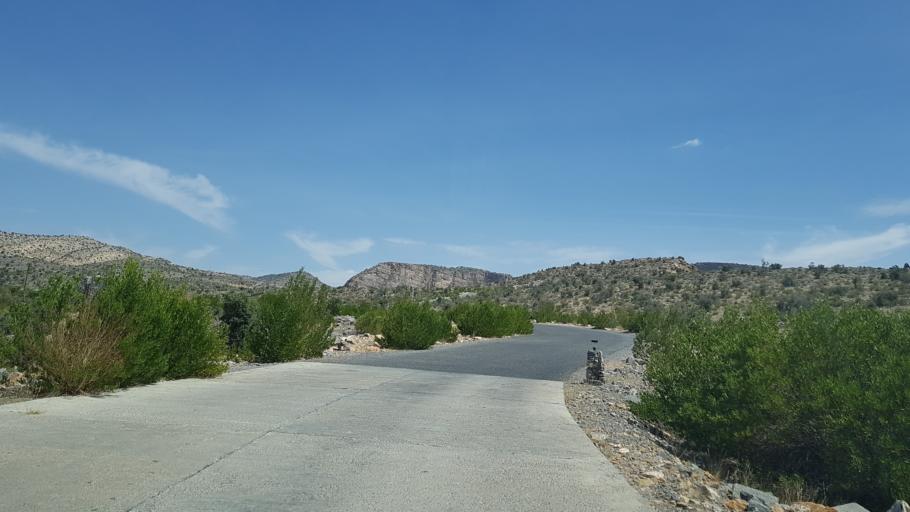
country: OM
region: Al Batinah
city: Bayt al `Awabi
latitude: 23.1408
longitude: 57.5388
